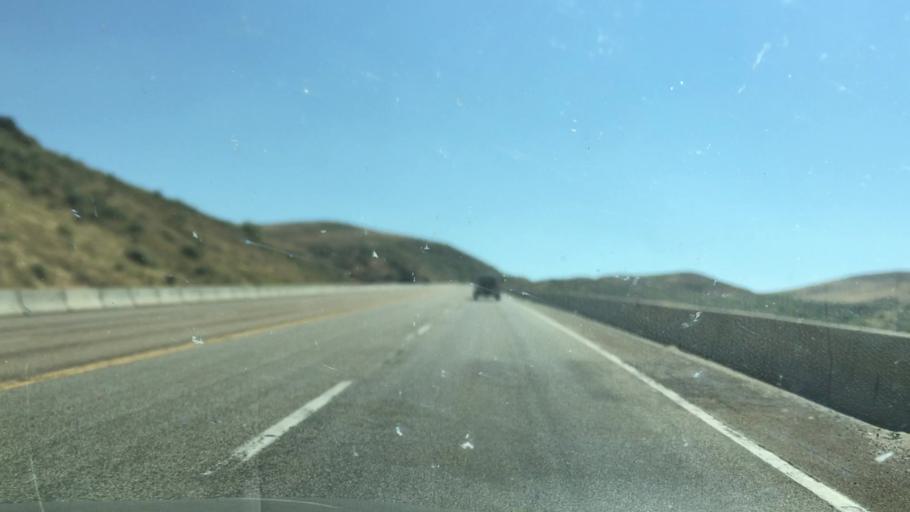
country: US
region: Idaho
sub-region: Ada County
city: Eagle
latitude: 43.8431
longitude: -116.2341
